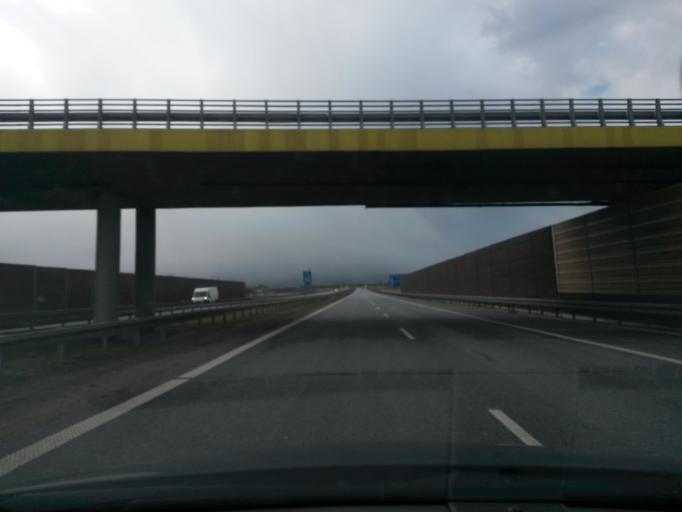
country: PL
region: Greater Poland Voivodeship
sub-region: Powiat koninski
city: Stare Miasto
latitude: 52.1612
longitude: 18.2294
